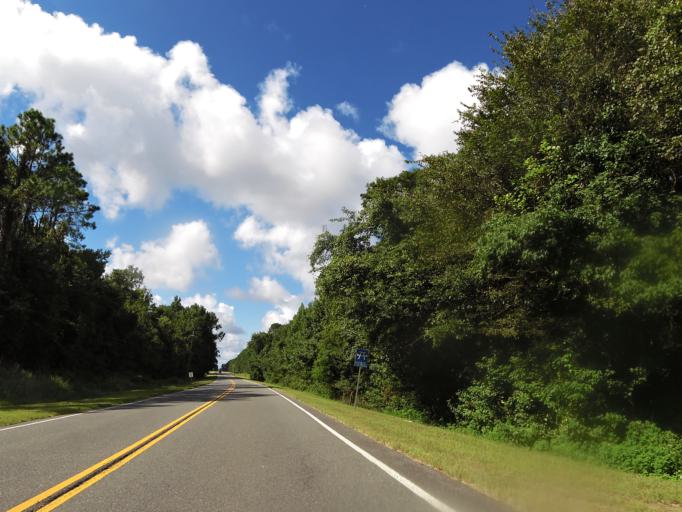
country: US
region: Georgia
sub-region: Camden County
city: Kingsland
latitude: 30.7821
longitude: -81.6867
